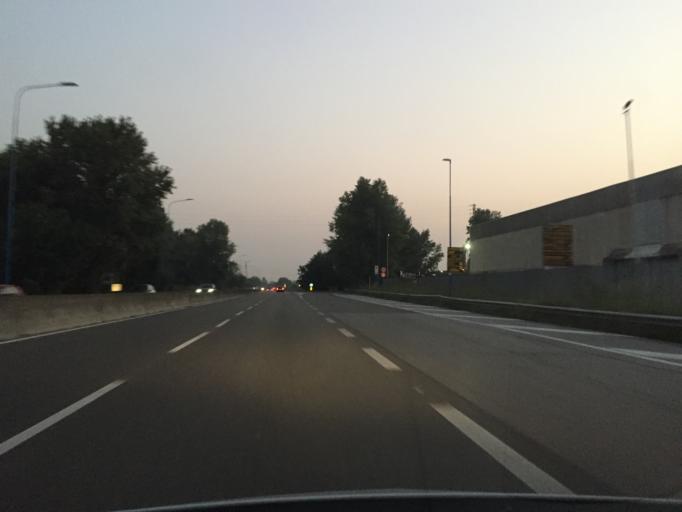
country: IT
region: Lombardy
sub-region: Provincia di Brescia
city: Roncadelle
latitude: 45.5152
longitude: 10.1698
